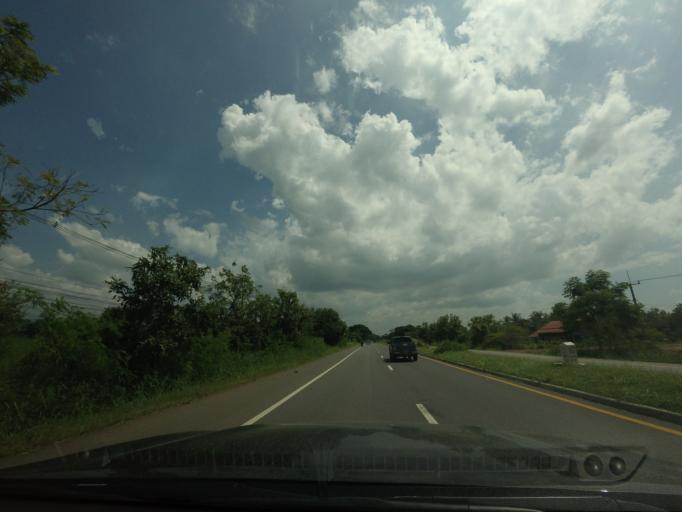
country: TH
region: Phetchabun
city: Phetchabun
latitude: 16.2296
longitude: 101.0858
